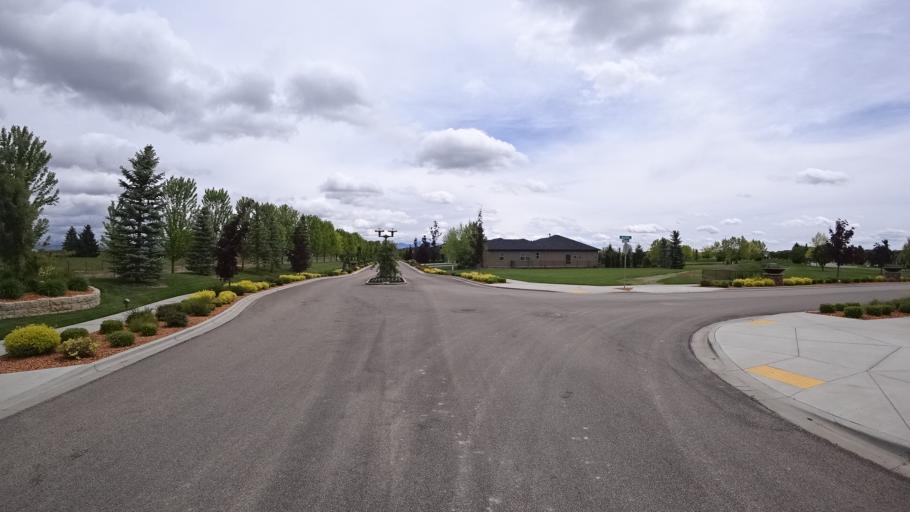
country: US
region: Idaho
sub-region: Ada County
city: Star
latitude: 43.7058
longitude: -116.4271
